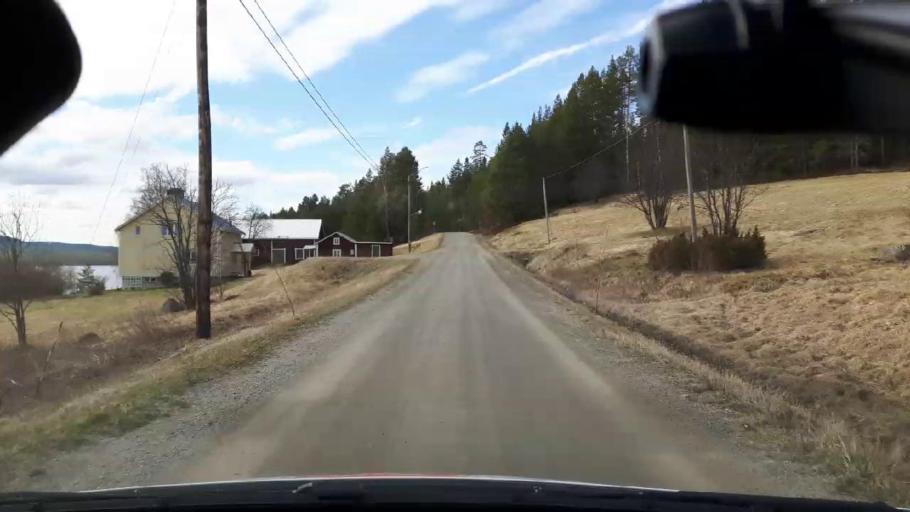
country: SE
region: Jaemtland
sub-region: Bergs Kommun
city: Hoverberg
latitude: 62.7195
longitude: 14.6766
